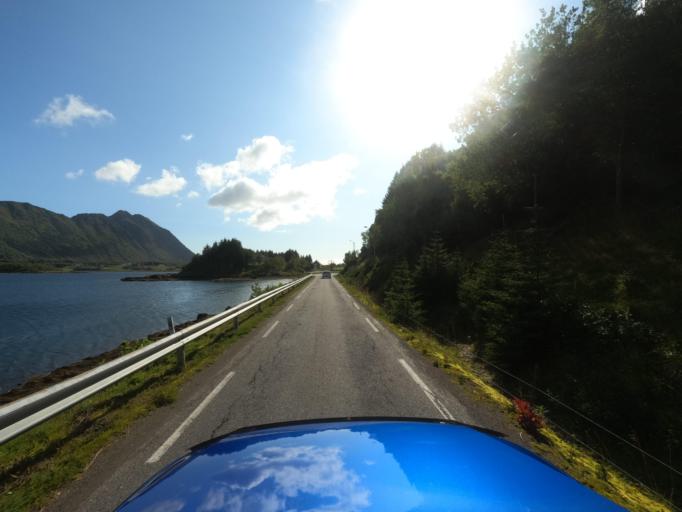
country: NO
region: Nordland
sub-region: Vestvagoy
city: Evjen
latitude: 68.1464
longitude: 13.7463
